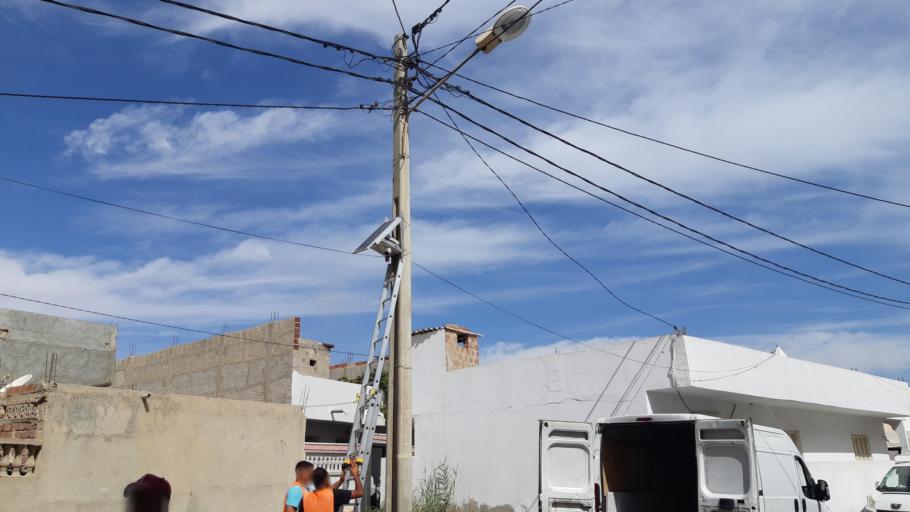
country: TN
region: Qabis
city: Gabes
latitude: 33.8958
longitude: 10.0928
